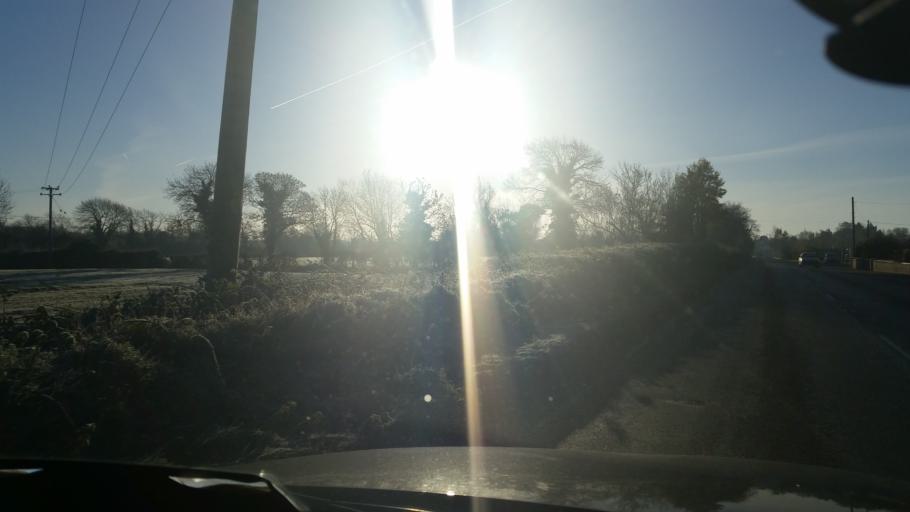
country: IE
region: Leinster
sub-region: Loch Garman
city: Gorey
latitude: 52.6161
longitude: -6.3068
